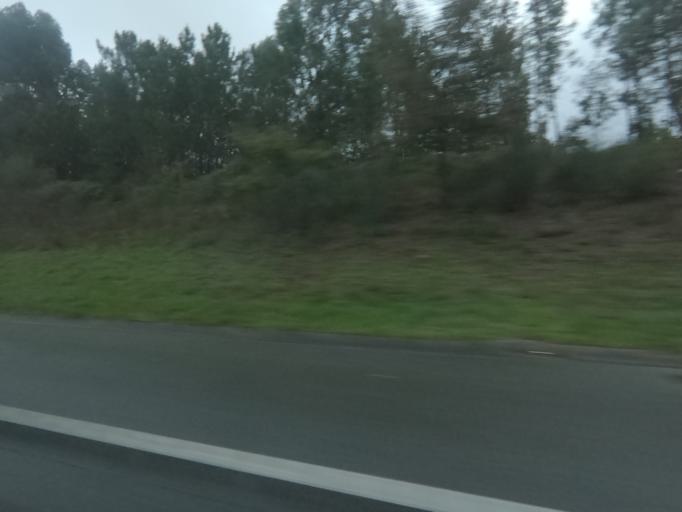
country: PT
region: Braga
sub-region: Barcelos
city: Galegos
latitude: 41.6175
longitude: -8.5527
